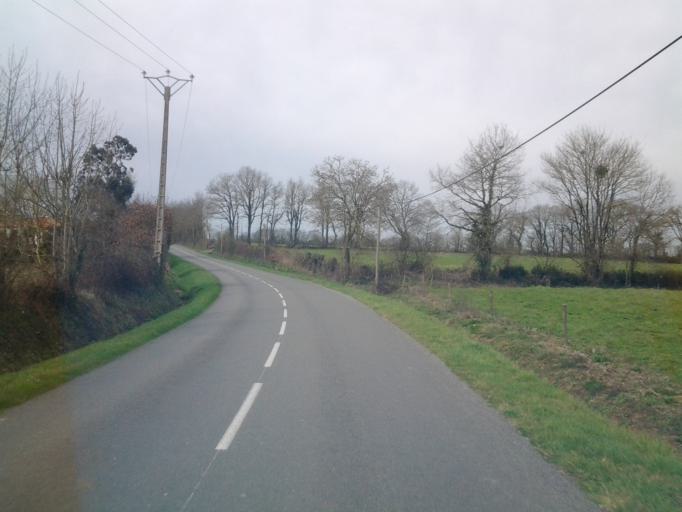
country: FR
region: Pays de la Loire
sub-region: Departement de la Vendee
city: Venansault
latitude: 46.6869
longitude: -1.5325
